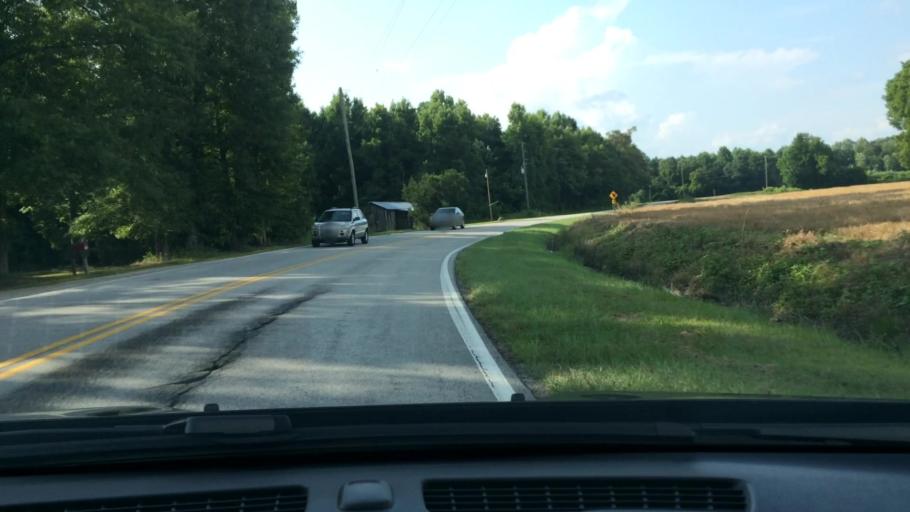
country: US
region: North Carolina
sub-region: Beaufort County
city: River Road
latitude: 35.4550
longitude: -77.0207
